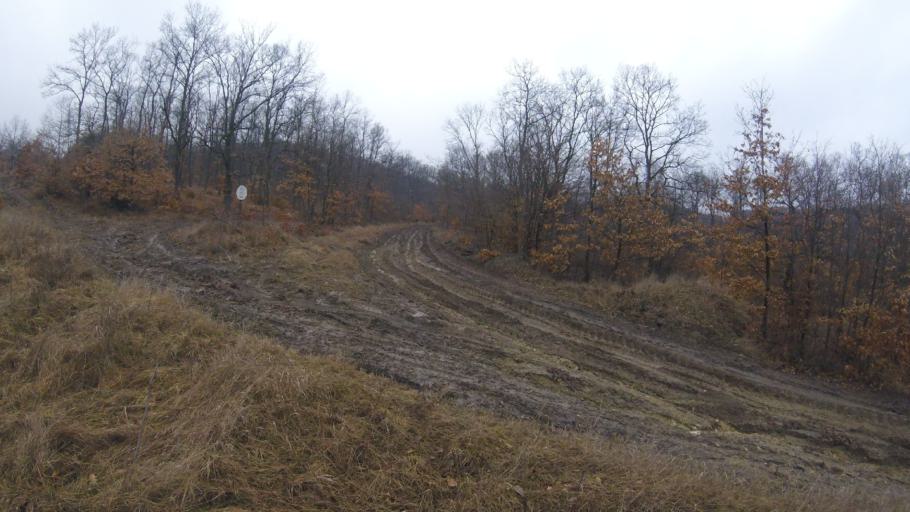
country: HU
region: Borsod-Abauj-Zemplen
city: Saly
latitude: 47.9671
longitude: 20.6001
